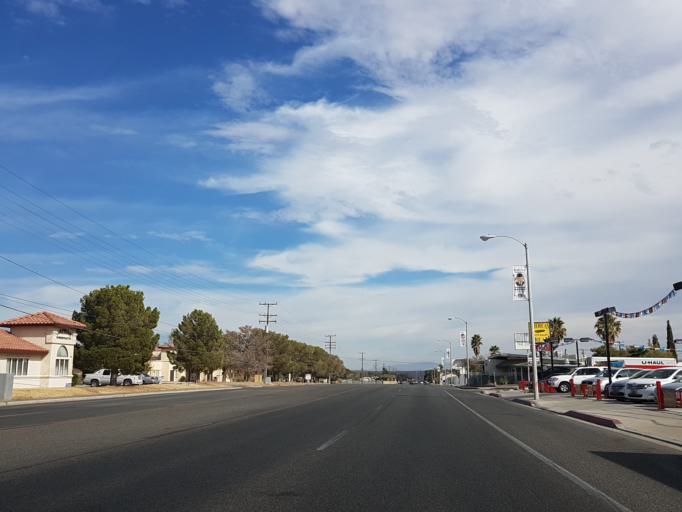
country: US
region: California
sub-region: Kern County
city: Ridgecrest
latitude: 35.6225
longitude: -117.6665
